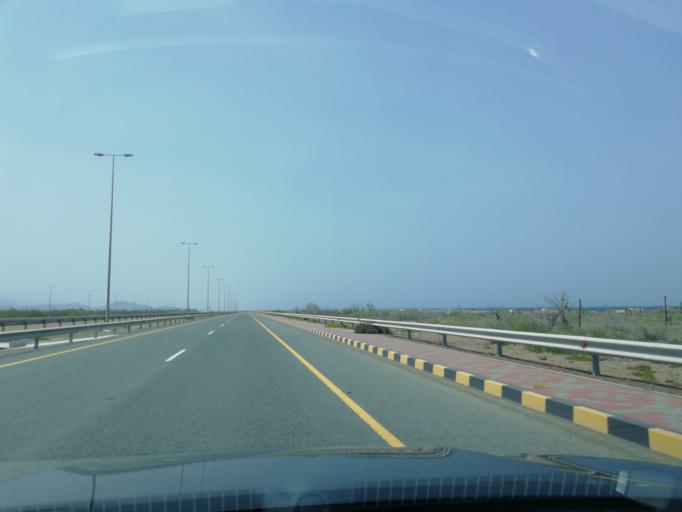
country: OM
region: Al Batinah
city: Shinas
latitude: 24.8813
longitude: 56.4040
